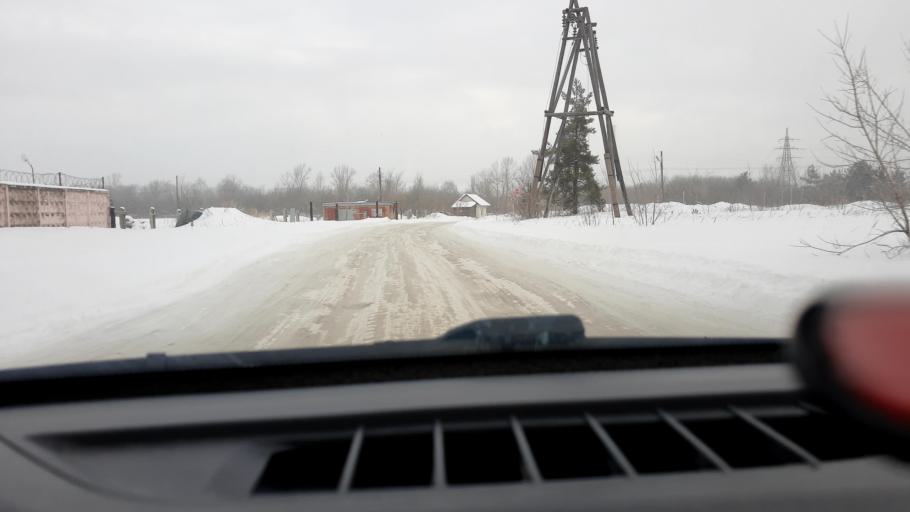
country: RU
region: Nizjnij Novgorod
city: Babino
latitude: 56.2612
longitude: 43.6117
